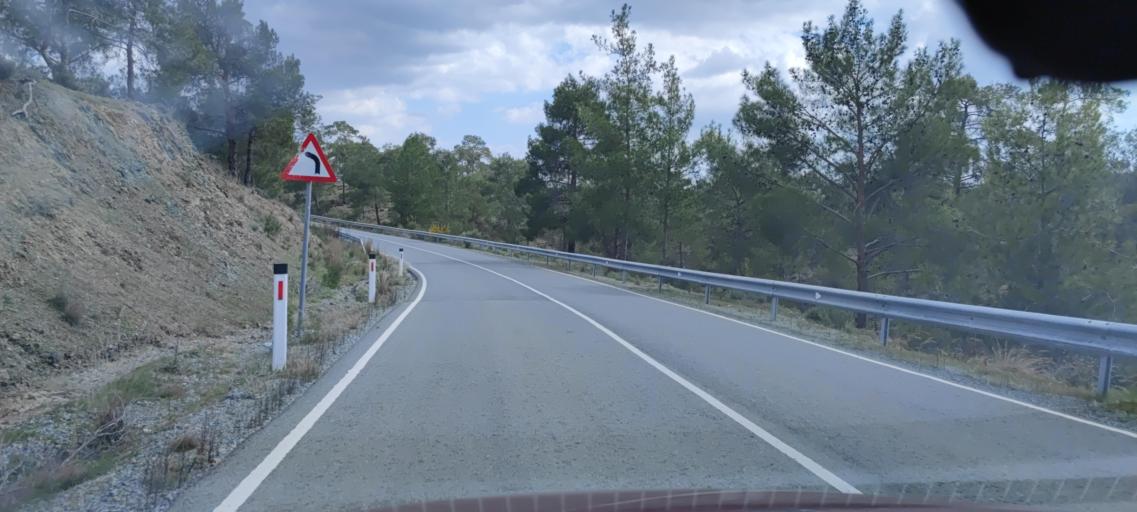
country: CY
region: Lefkosia
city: Lythrodontas
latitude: 34.9294
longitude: 33.3374
